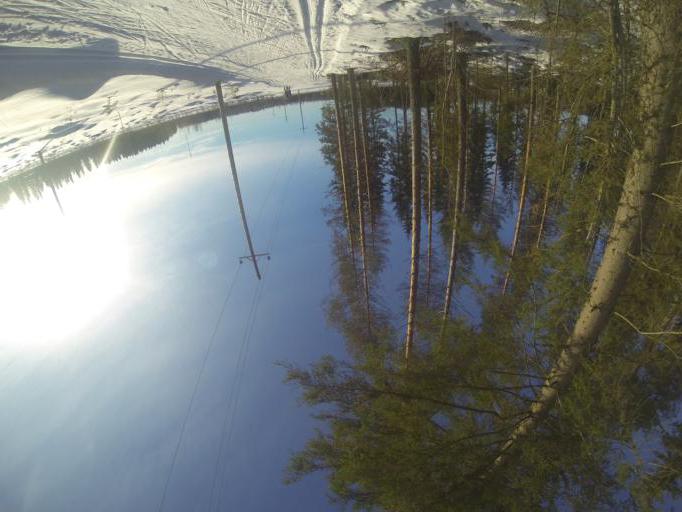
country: FI
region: Southern Savonia
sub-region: Savonlinna
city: Savonlinna
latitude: 61.9211
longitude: 28.9048
